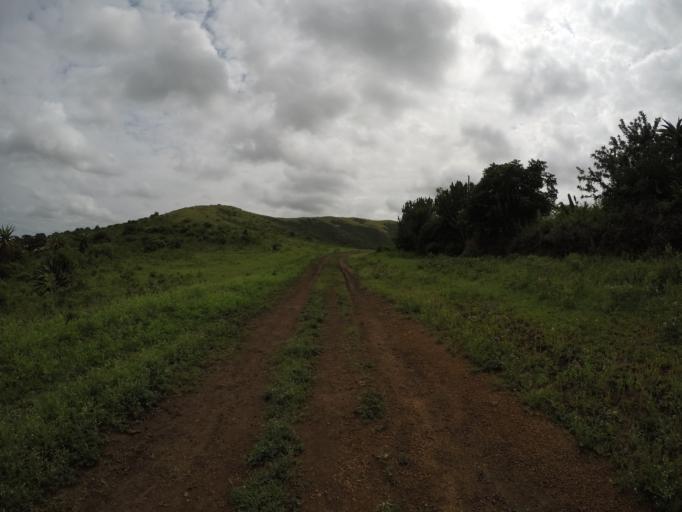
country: ZA
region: KwaZulu-Natal
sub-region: uThungulu District Municipality
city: Empangeni
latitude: -28.6115
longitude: 31.8995
